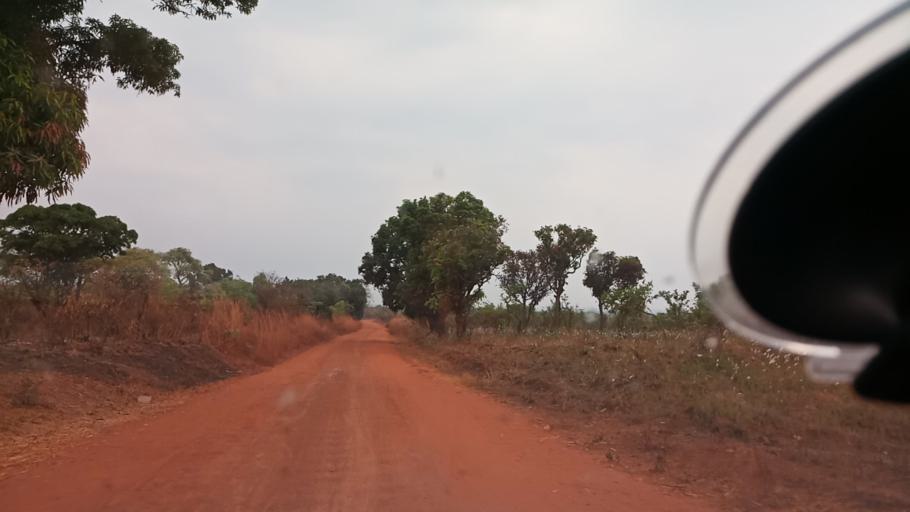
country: ZM
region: Luapula
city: Nchelenge
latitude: -9.1758
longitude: 28.2818
